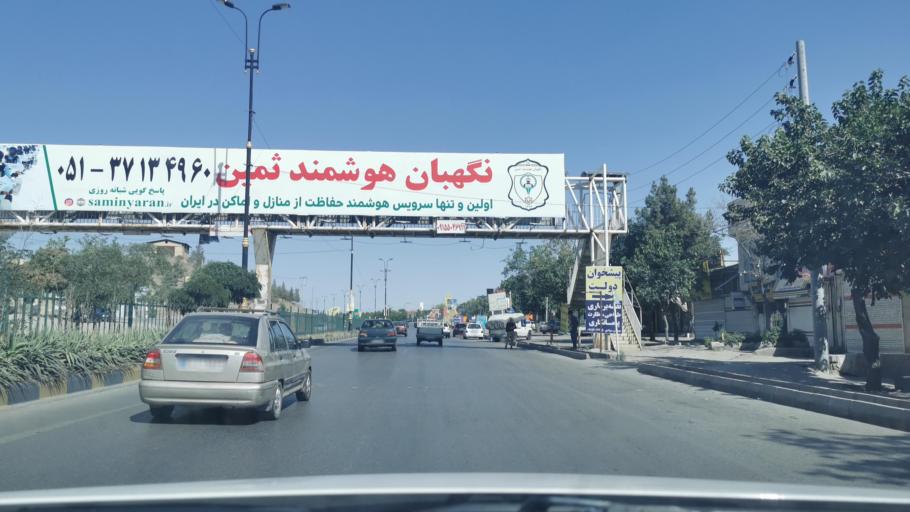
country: IR
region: Razavi Khorasan
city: Torqabeh
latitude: 36.4012
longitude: 59.3886
